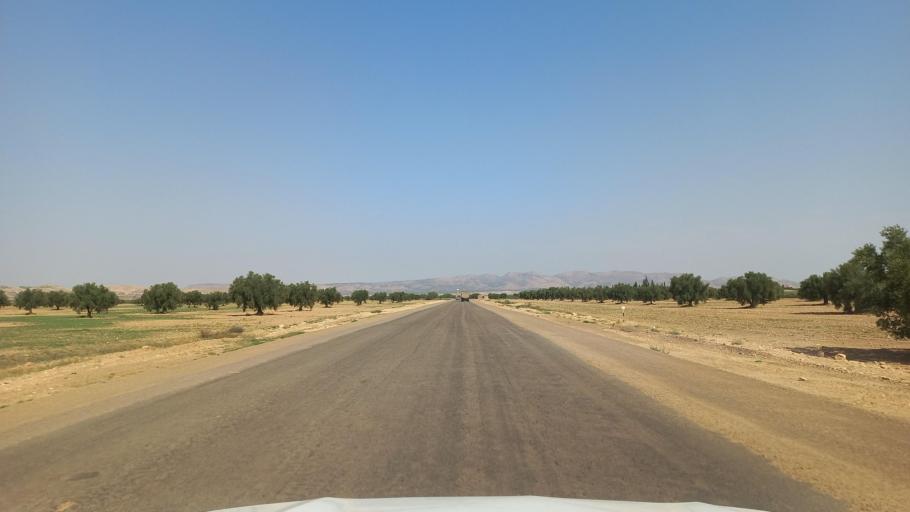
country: TN
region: Al Qasrayn
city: Sbiba
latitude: 35.3435
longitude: 9.0555
